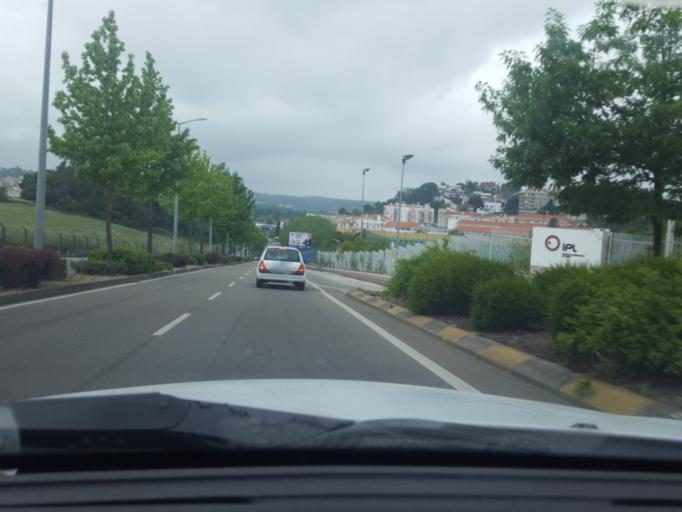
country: PT
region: Leiria
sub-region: Leiria
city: Leiria
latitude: 39.7361
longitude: -8.8114
